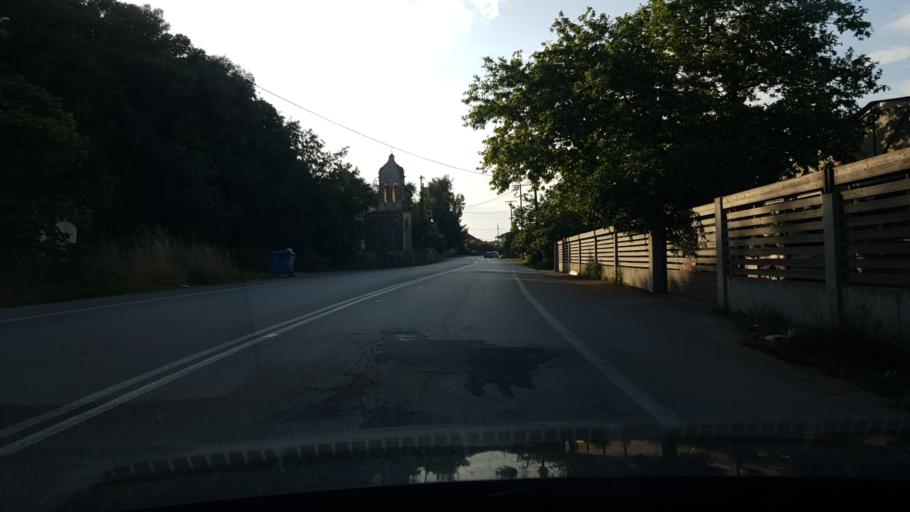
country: GR
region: Ionian Islands
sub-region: Lefkada
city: Lefkada
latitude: 38.8153
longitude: 20.7053
